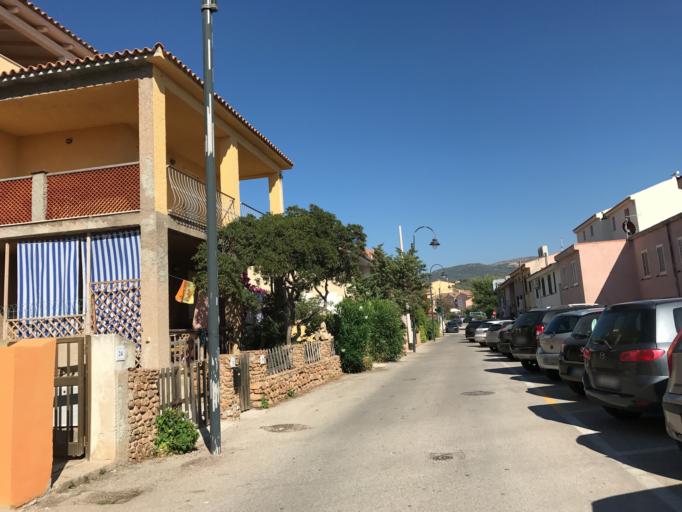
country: IT
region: Sardinia
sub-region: Provincia di Olbia-Tempio
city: Trinita d'Agultu
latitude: 41.0134
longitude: 8.8741
